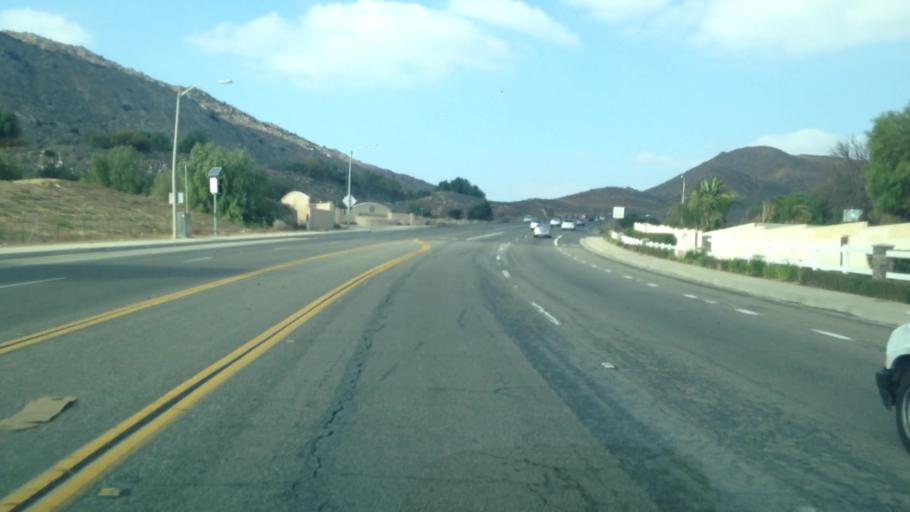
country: US
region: California
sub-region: Riverside County
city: Sunnyslope
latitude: 34.0273
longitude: -117.4290
